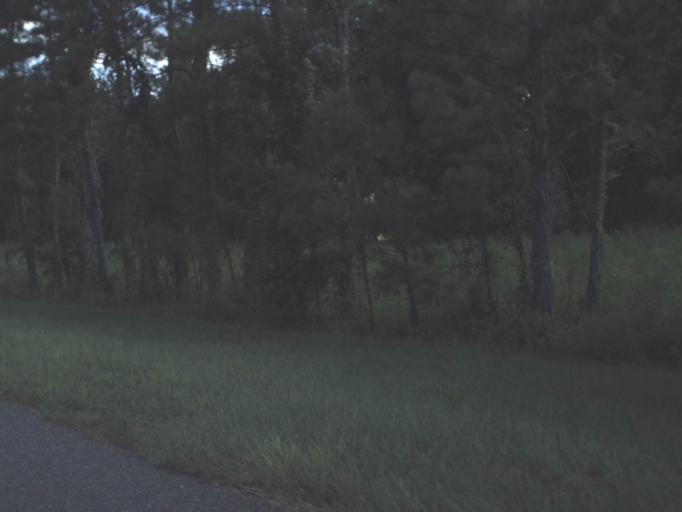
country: US
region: Florida
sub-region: Levy County
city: Chiefland
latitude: 29.4417
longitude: -82.8384
